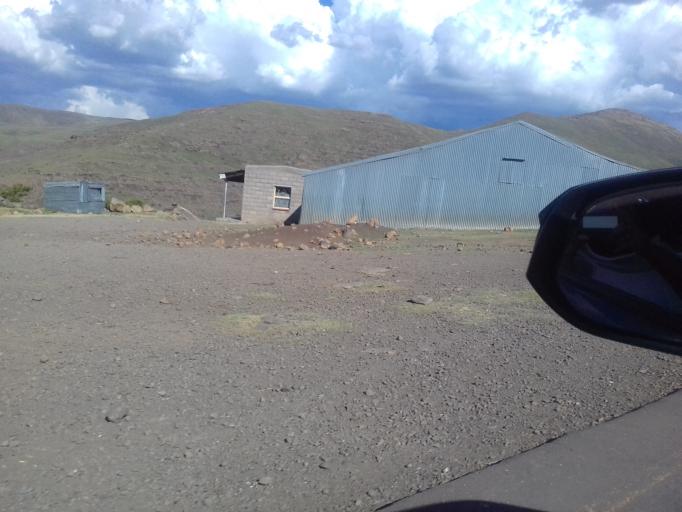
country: LS
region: Thaba-Tseka
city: Thaba-Tseka
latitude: -29.5141
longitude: 28.3245
